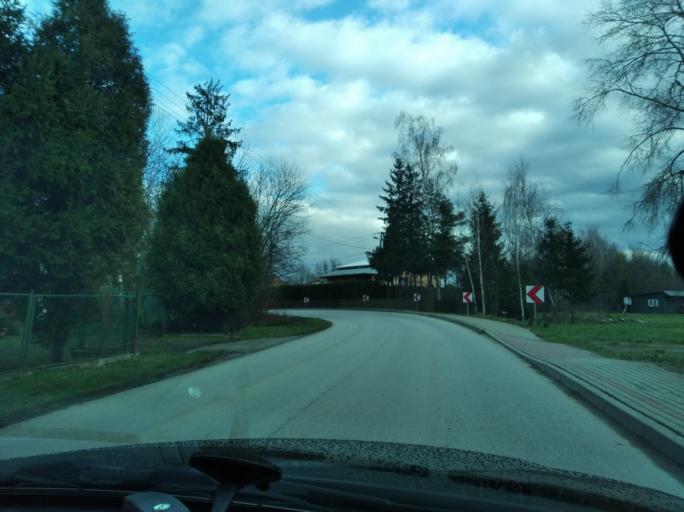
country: PL
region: Subcarpathian Voivodeship
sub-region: Powiat lancucki
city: Gluchow
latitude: 50.1003
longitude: 22.2775
